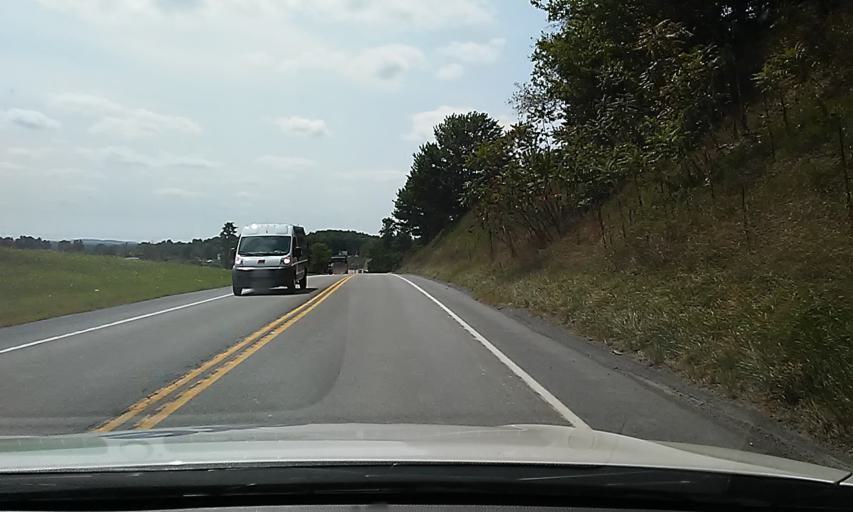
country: US
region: Pennsylvania
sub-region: Jefferson County
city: Punxsutawney
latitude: 40.9117
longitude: -78.9987
